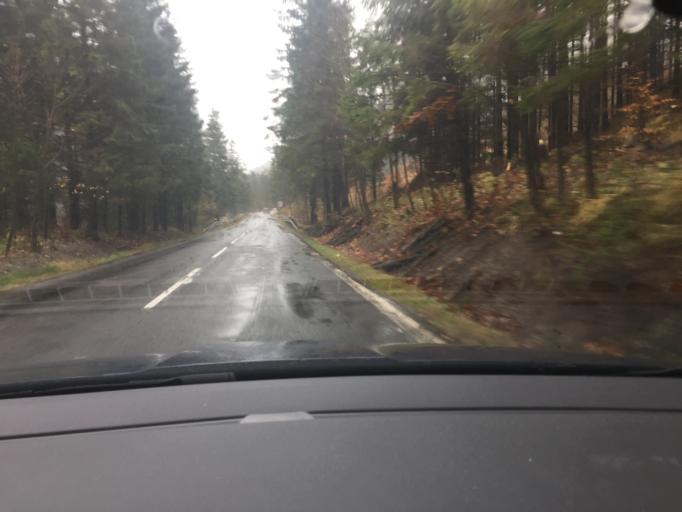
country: SK
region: Presovsky
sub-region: Okres Poprad
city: Zdiar
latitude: 49.2423
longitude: 20.3097
